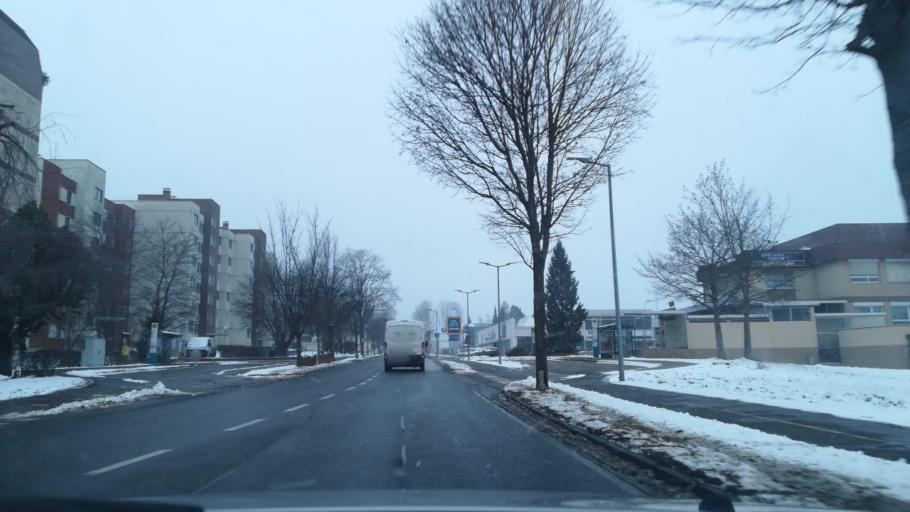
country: AT
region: Styria
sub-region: Politischer Bezirk Murtal
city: Oberweg
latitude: 47.1705
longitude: 14.6419
